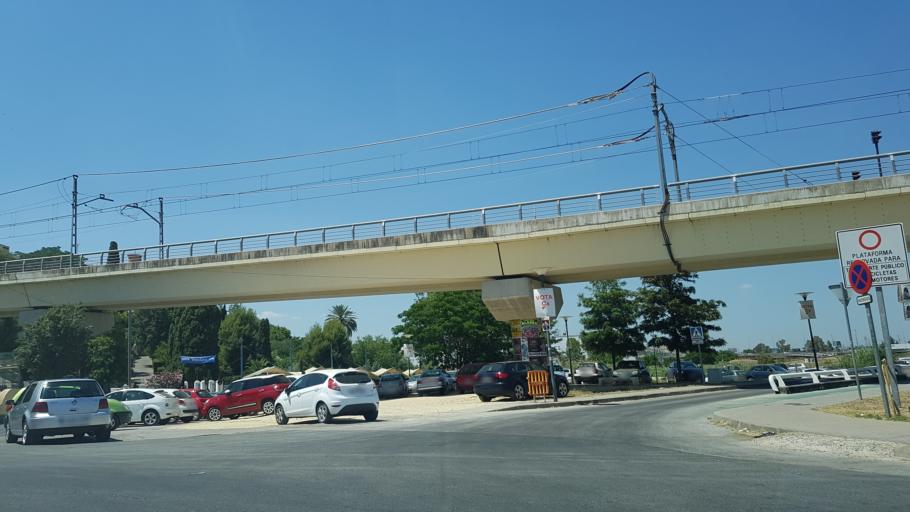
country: ES
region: Andalusia
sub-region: Provincia de Sevilla
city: San Juan de Aznalfarache
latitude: 37.3664
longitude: -6.0257
